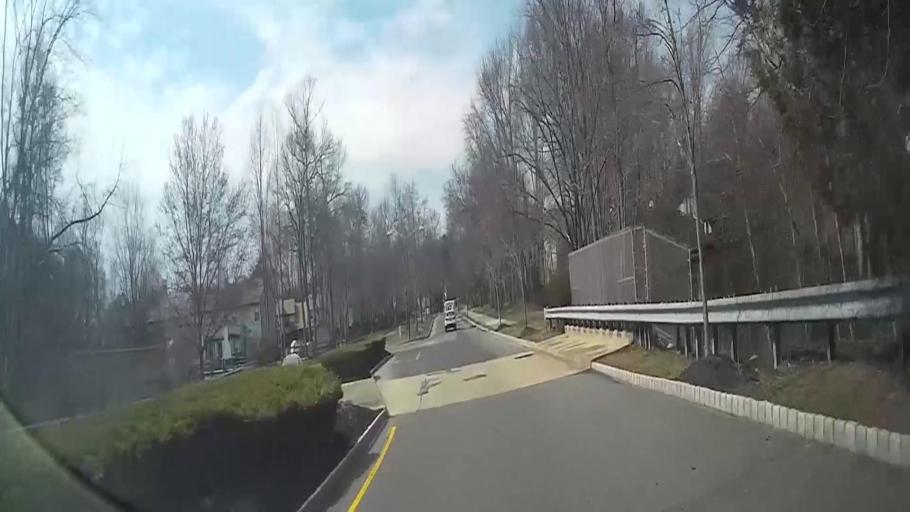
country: US
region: New Jersey
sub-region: Burlington County
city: Marlton
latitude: 39.8719
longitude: -74.8648
